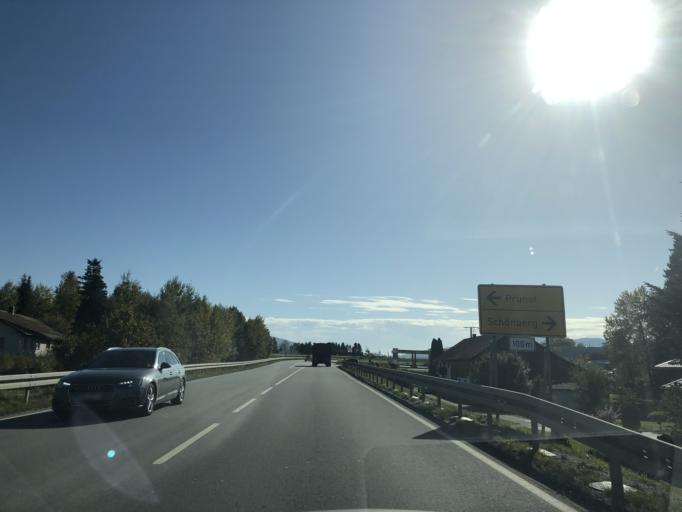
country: DE
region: Bavaria
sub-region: Lower Bavaria
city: Patersdorf
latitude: 49.0087
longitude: 12.9830
